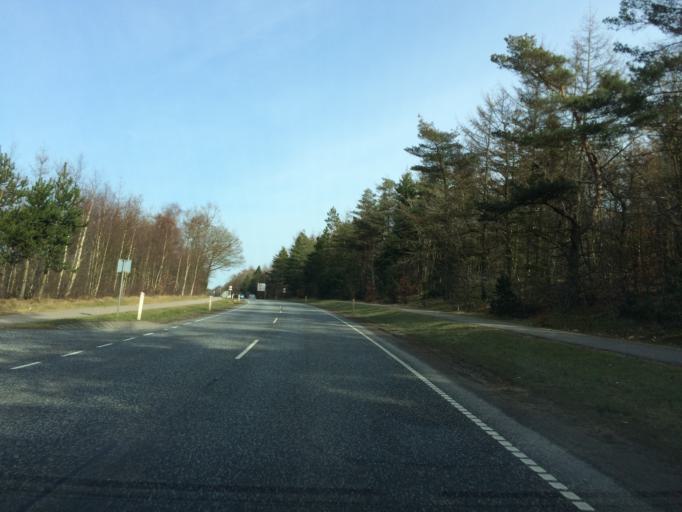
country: DK
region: Central Jutland
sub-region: Holstebro Kommune
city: Holstebro
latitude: 56.3433
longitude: 8.6256
